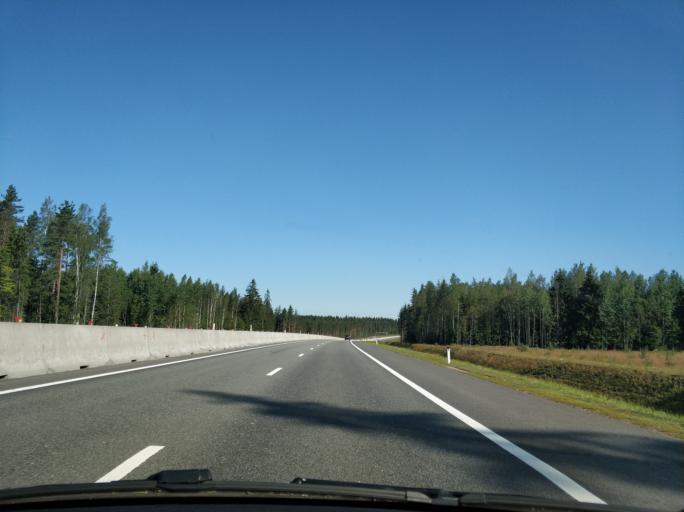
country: RU
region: Leningrad
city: Sosnovo
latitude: 60.5261
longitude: 30.1669
